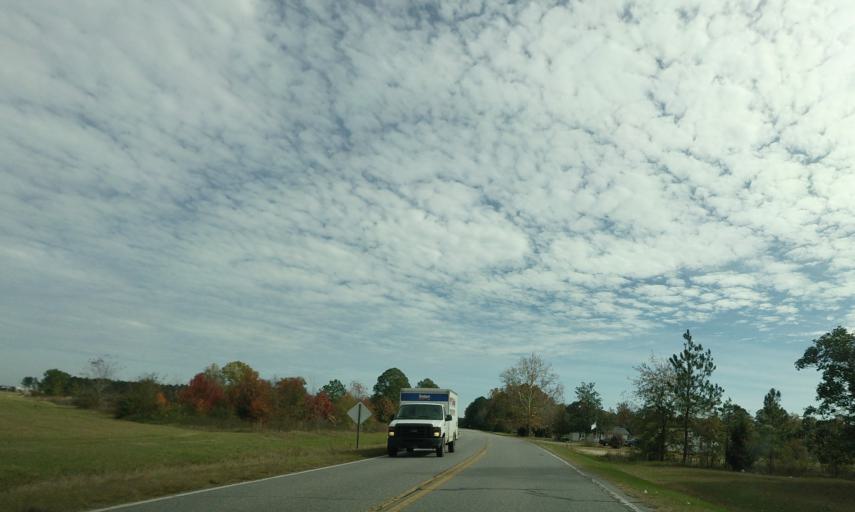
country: US
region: Georgia
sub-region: Bleckley County
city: Cochran
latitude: 32.3948
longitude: -83.2805
